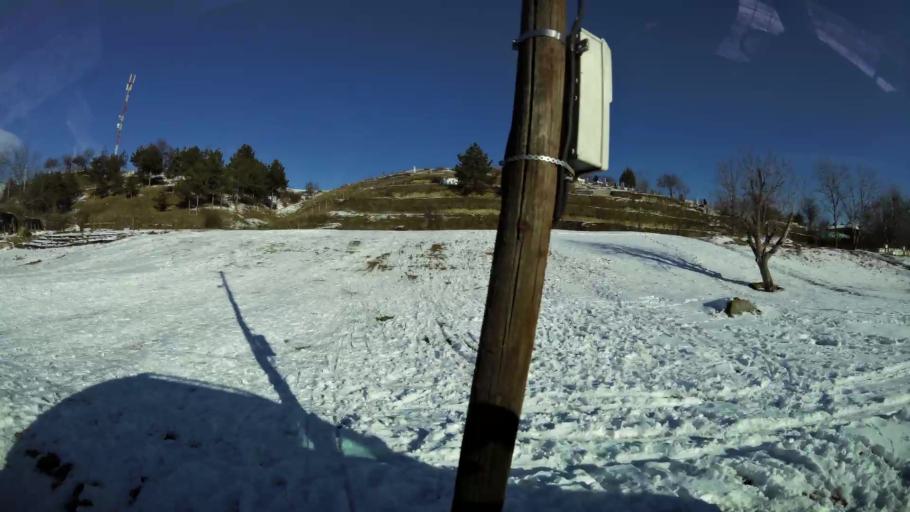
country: MK
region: Saraj
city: Saraj
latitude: 42.0111
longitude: 21.3412
